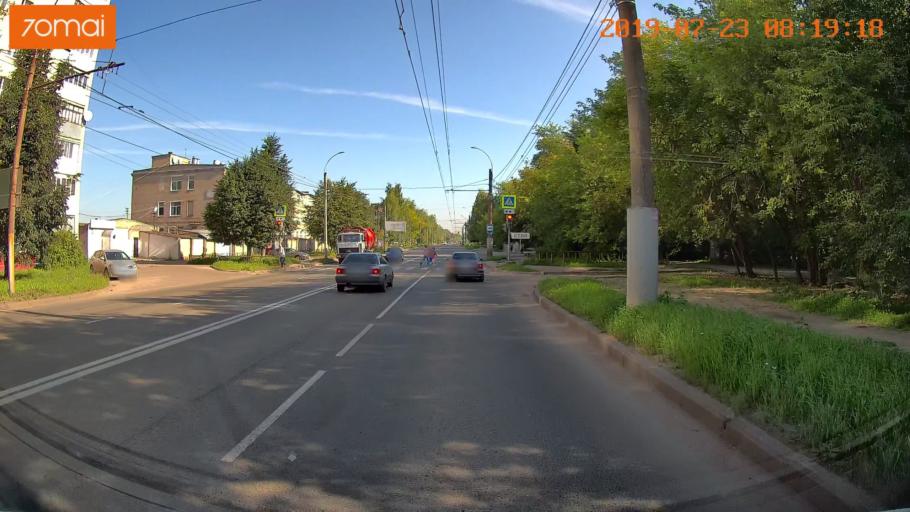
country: RU
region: Ivanovo
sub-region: Gorod Ivanovo
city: Ivanovo
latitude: 56.9672
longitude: 40.9629
